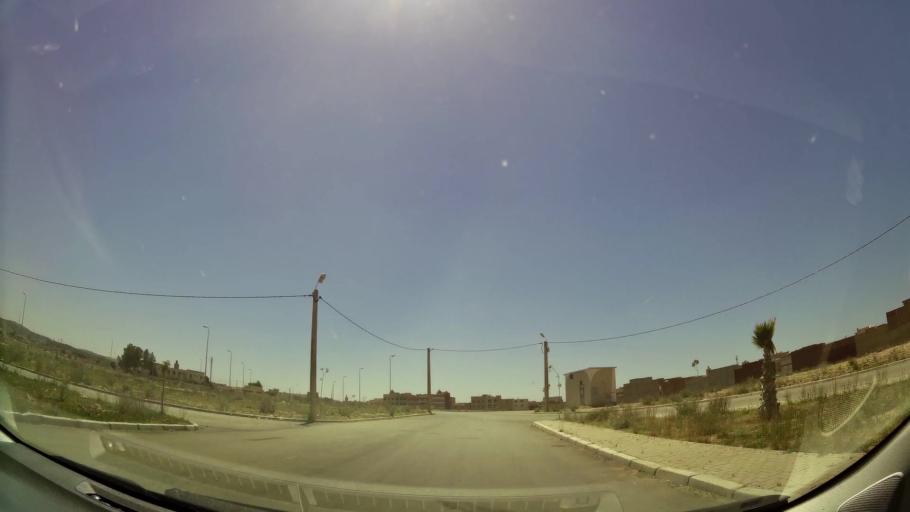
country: MA
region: Oriental
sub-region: Oujda-Angad
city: Oujda
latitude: 34.6686
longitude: -1.8657
